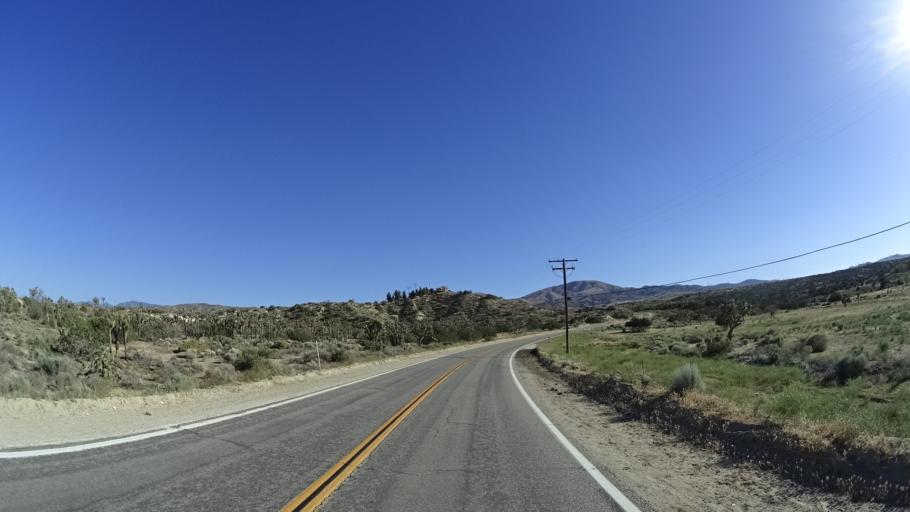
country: US
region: California
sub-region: Los Angeles County
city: Littlerock
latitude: 34.5196
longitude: -118.0278
